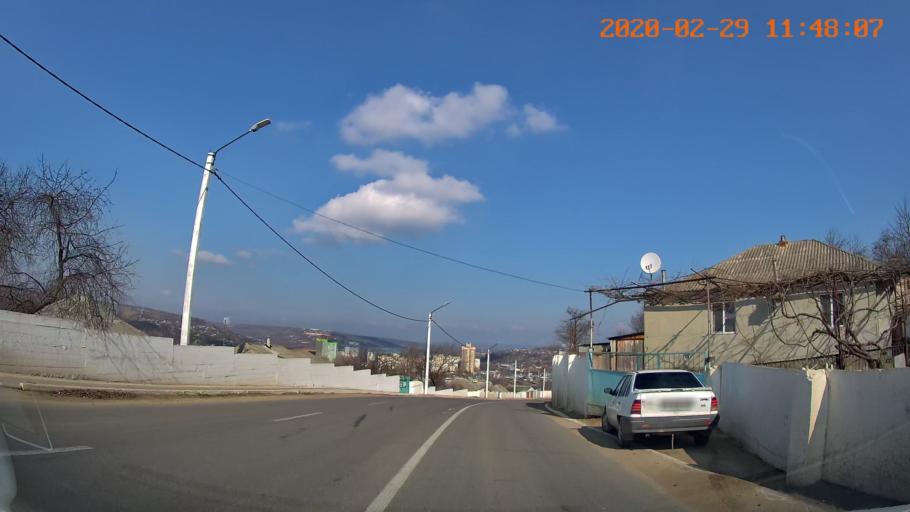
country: MD
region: Rezina
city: Rezina
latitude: 47.7460
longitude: 28.9890
